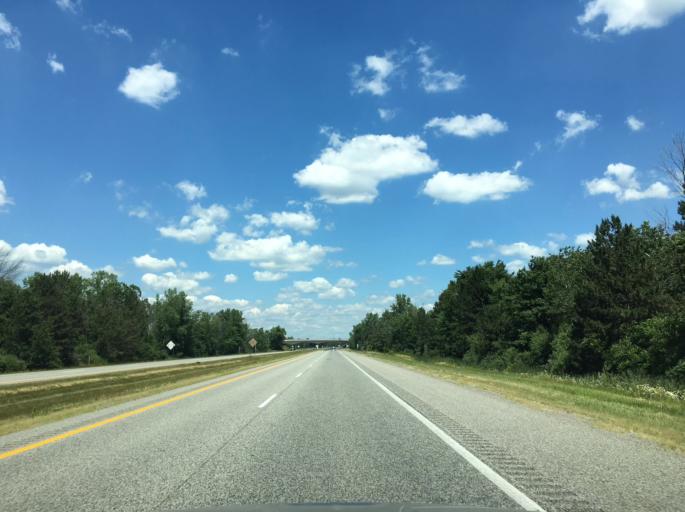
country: US
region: Michigan
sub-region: Midland County
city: Midland
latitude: 43.6365
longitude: -84.1842
